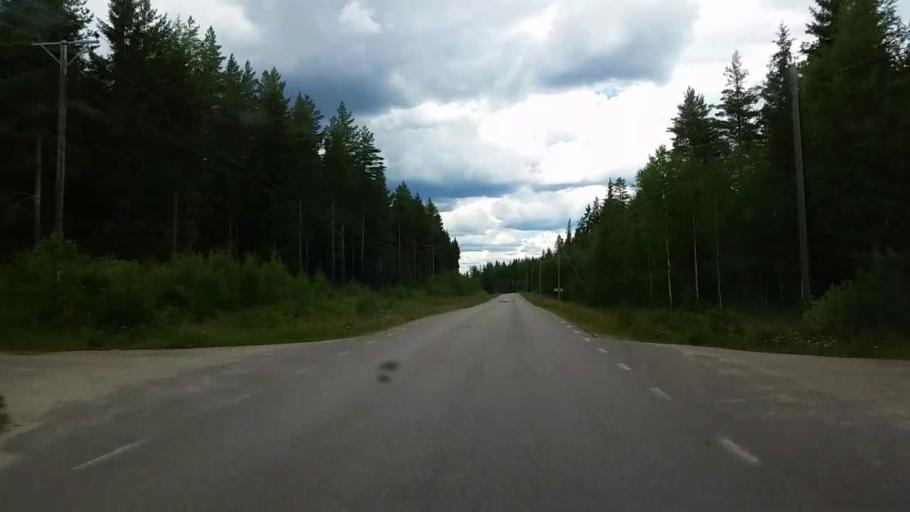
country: SE
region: Gaevleborg
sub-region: Ovanakers Kommun
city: Edsbyn
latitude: 61.4293
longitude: 15.8990
